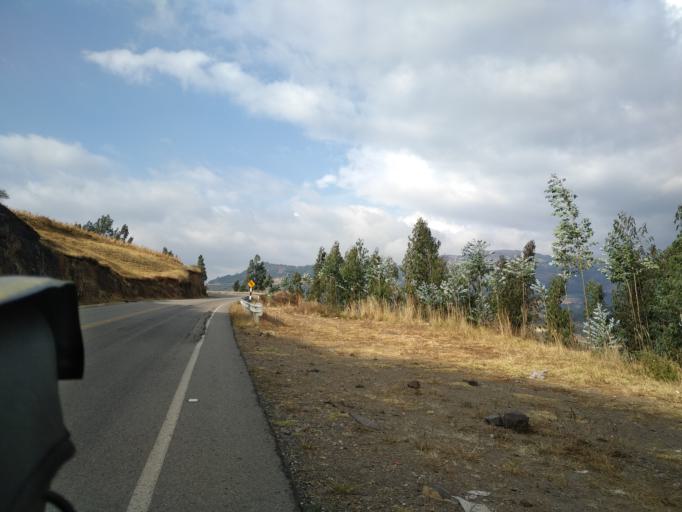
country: PE
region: La Libertad
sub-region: Provincia de Otuzco
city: Agallpampa
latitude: -7.9899
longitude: -78.5348
